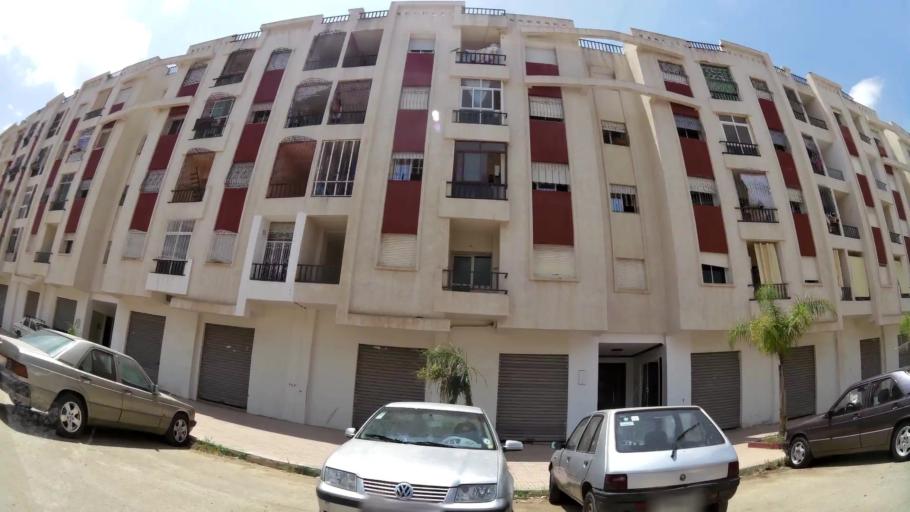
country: MA
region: Rabat-Sale-Zemmour-Zaer
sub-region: Khemisset
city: Tiflet
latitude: 34.0104
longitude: -6.5259
